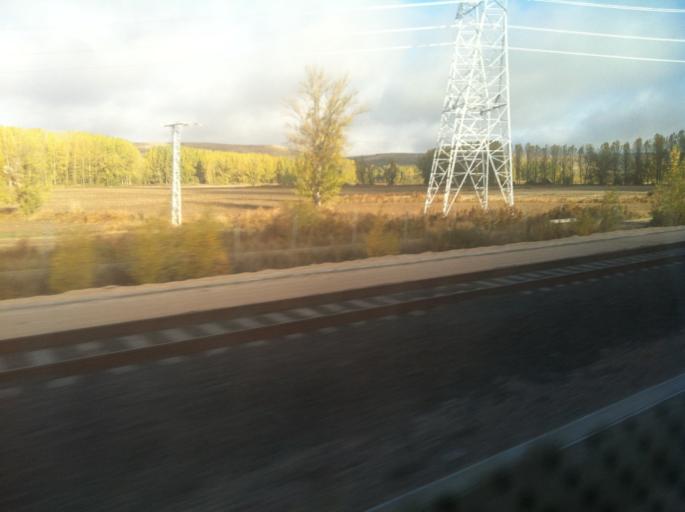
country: ES
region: Castille and Leon
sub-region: Provincia de Burgos
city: San Mames de Burgos
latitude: 42.3384
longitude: -3.7972
